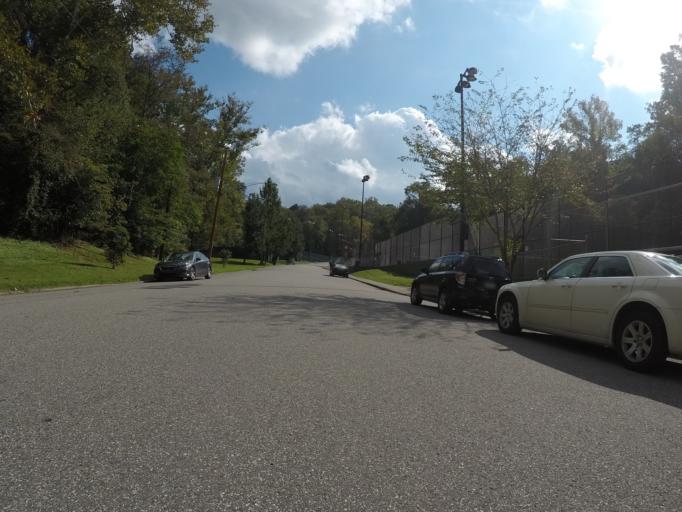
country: US
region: West Virginia
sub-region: Cabell County
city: Huntington
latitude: 38.4072
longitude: -82.4346
